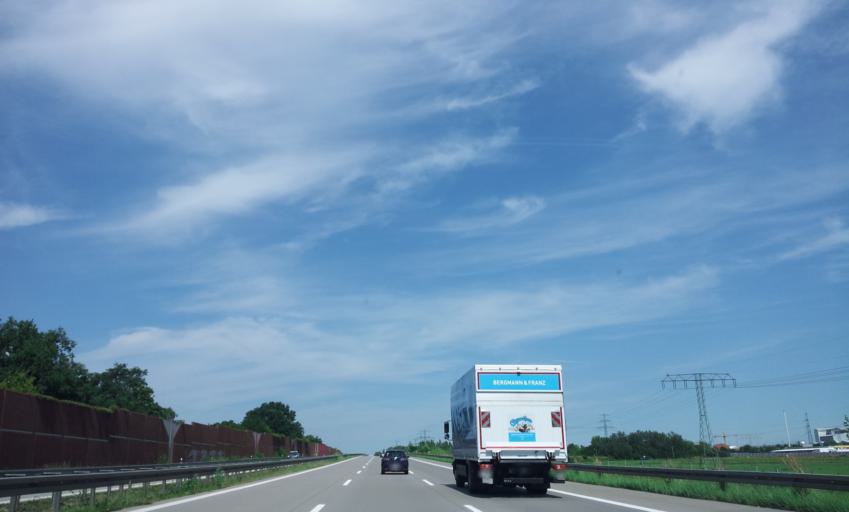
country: DE
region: Brandenburg
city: Neuenhagen
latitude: 52.5249
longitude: 13.7158
